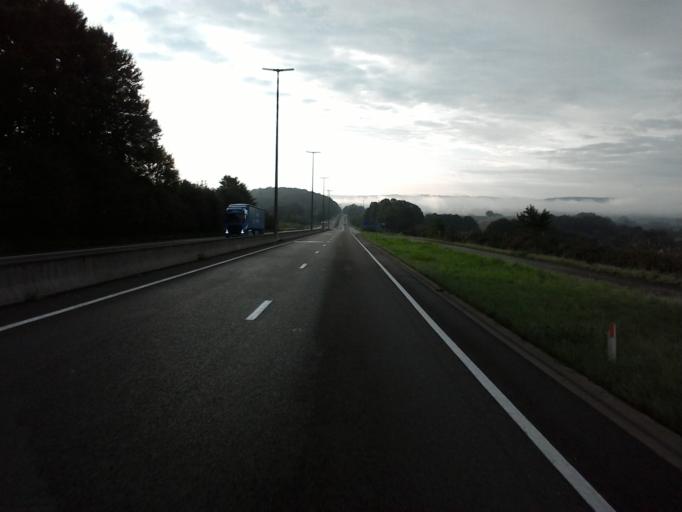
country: BE
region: Wallonia
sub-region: Province du Luxembourg
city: Attert
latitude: 49.7661
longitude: 5.7677
